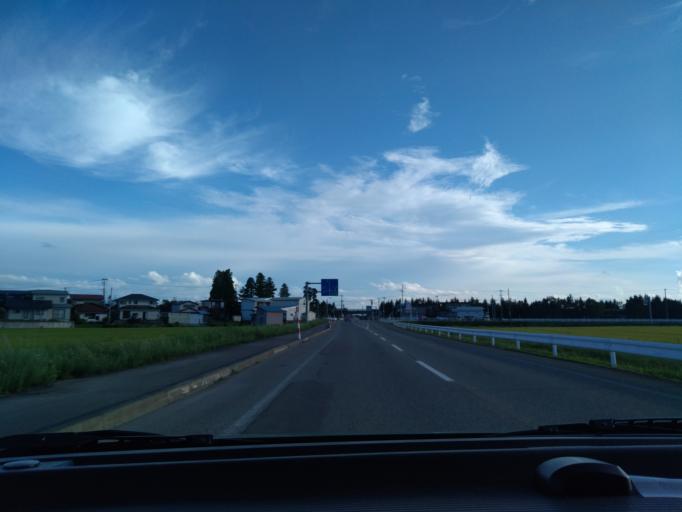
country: JP
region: Akita
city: Omagari
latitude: 39.4022
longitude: 140.4745
